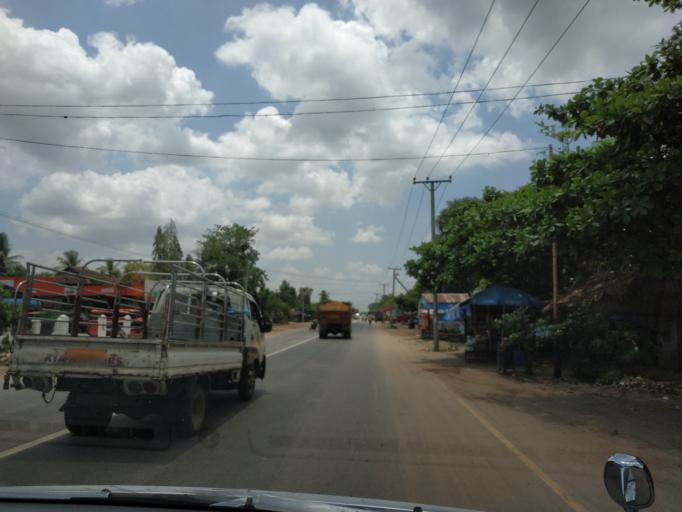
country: MM
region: Bago
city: Bago
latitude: 17.4740
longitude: 96.5312
